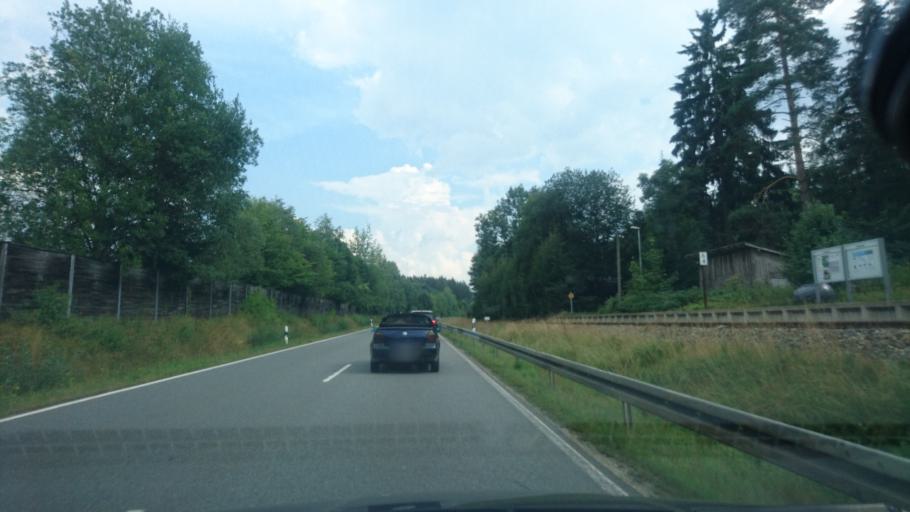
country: DE
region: Bavaria
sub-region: Lower Bavaria
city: Frauenau
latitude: 49.0068
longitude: 13.2770
